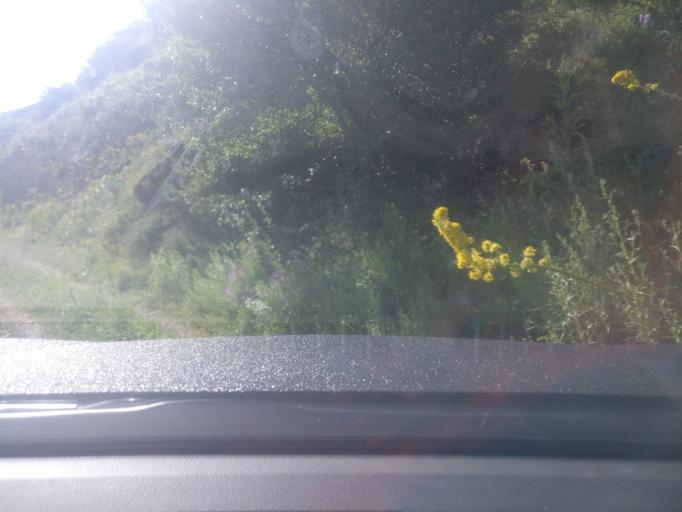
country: KZ
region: Almaty Qalasy
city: Almaty
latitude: 43.1072
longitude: 76.9416
